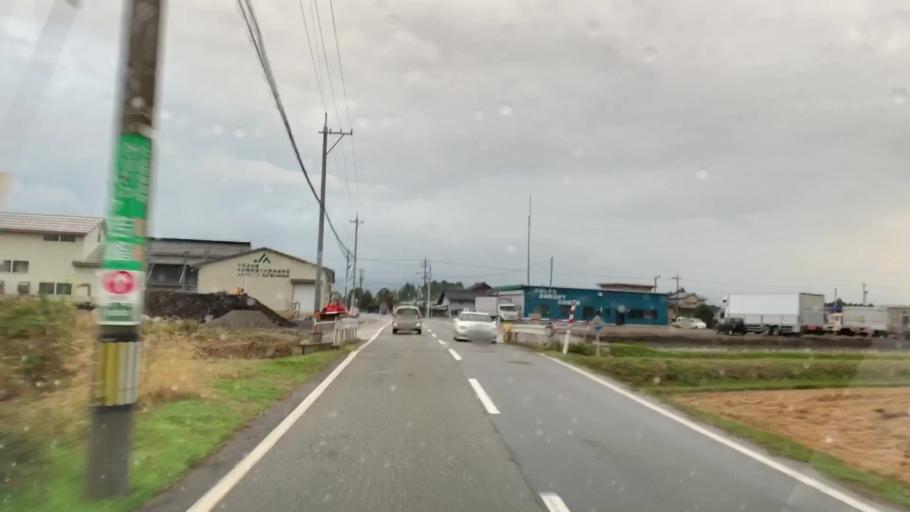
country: JP
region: Toyama
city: Kamiichi
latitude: 36.6482
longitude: 137.3281
